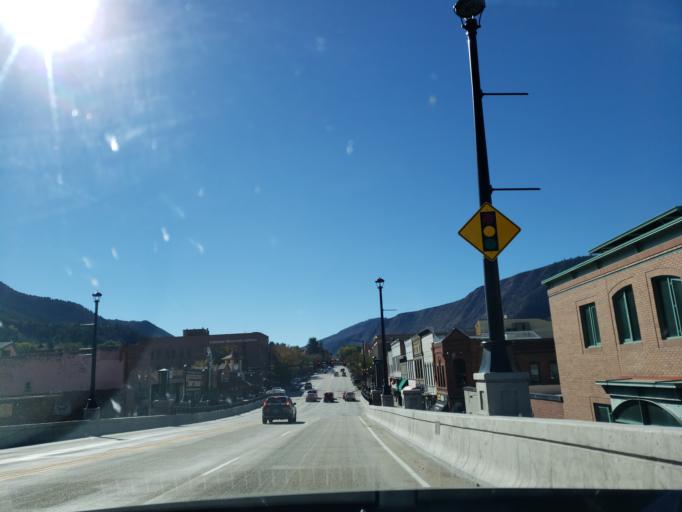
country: US
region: Colorado
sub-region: Garfield County
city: Glenwood Springs
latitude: 39.5478
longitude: -107.3247
